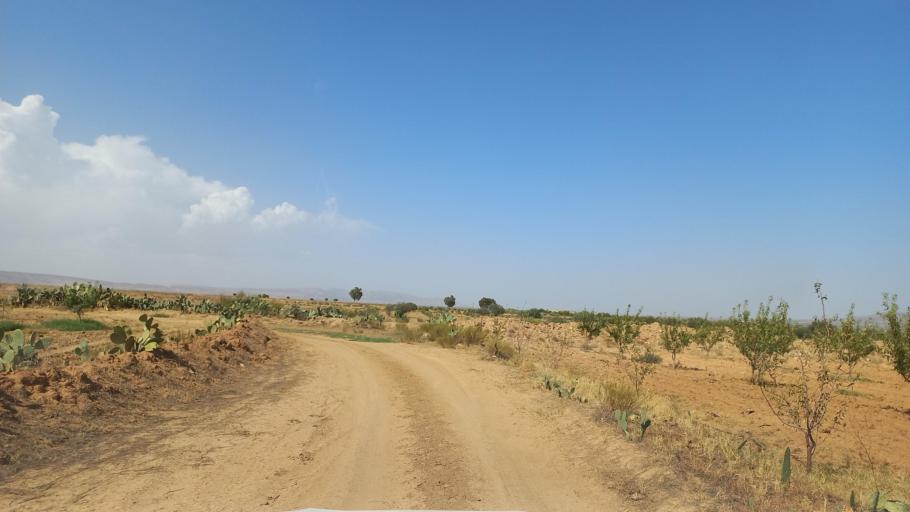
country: TN
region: Al Qasrayn
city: Kasserine
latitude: 35.2133
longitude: 9.0336
